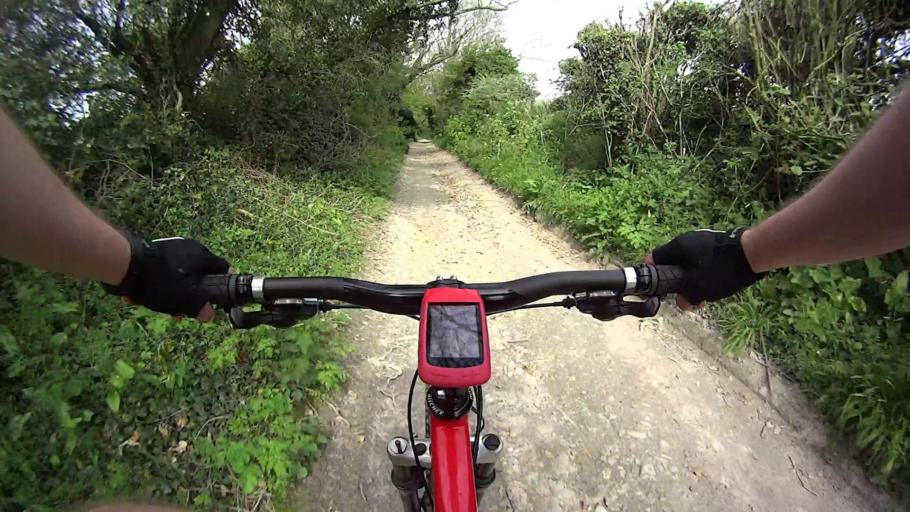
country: GB
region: England
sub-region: East Sussex
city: Seaford
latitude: 50.8087
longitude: 0.1712
